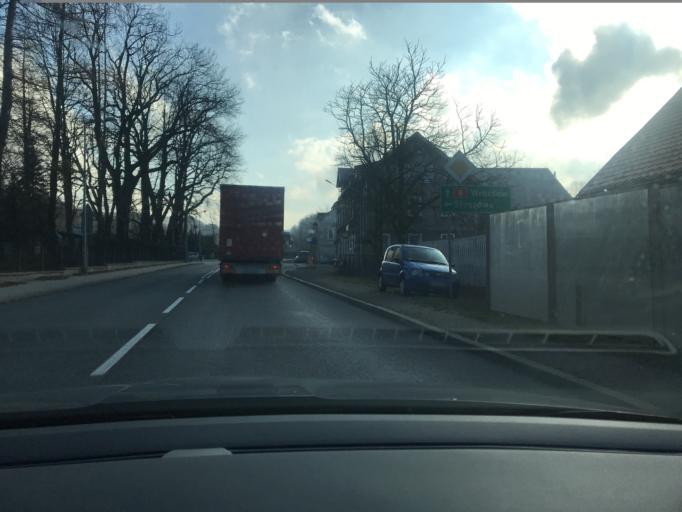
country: PL
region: Lower Silesian Voivodeship
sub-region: Powiat klodzki
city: Kudowa-Zdroj
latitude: 50.4226
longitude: 16.2581
